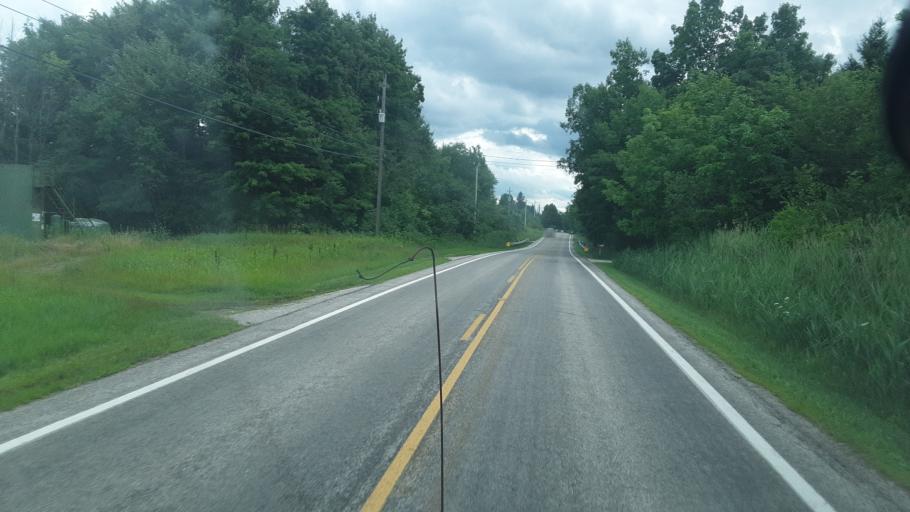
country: US
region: Ohio
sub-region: Ashtabula County
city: Jefferson
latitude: 41.7049
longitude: -80.7812
